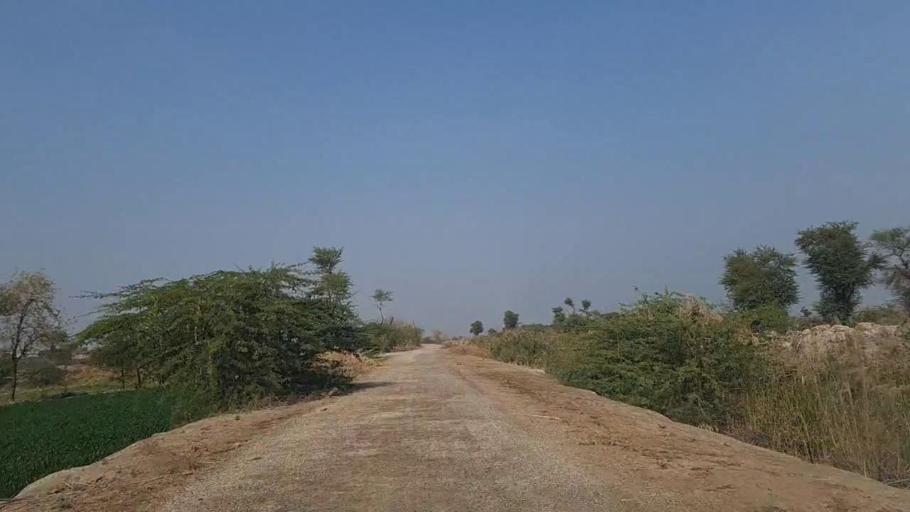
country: PK
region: Sindh
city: Nawabshah
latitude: 26.3692
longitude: 68.4255
